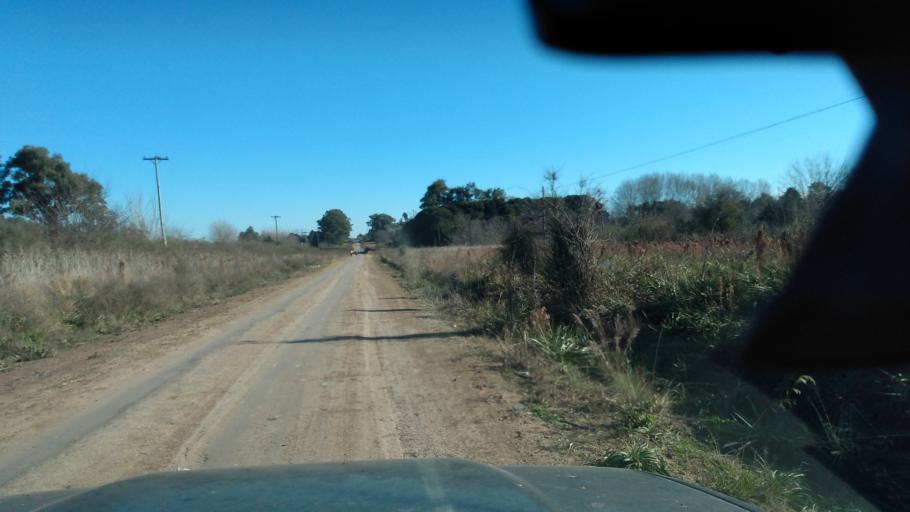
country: AR
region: Buenos Aires
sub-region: Partido de Lujan
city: Lujan
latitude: -34.5619
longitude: -59.1635
